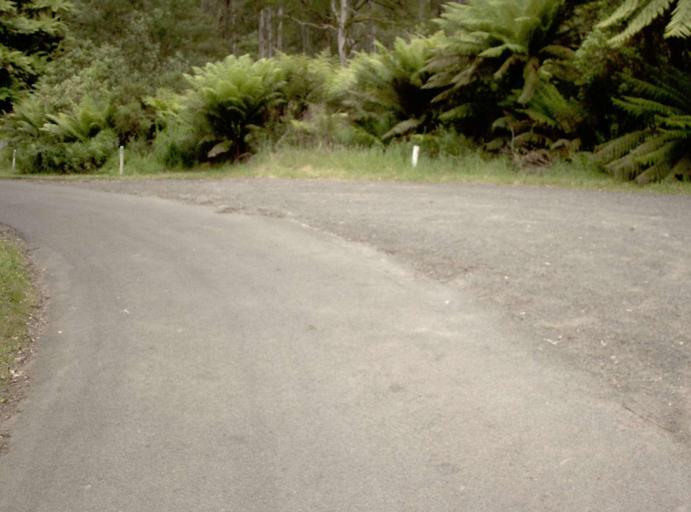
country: AU
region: Victoria
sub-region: Latrobe
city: Traralgon
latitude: -38.4543
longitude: 146.5412
